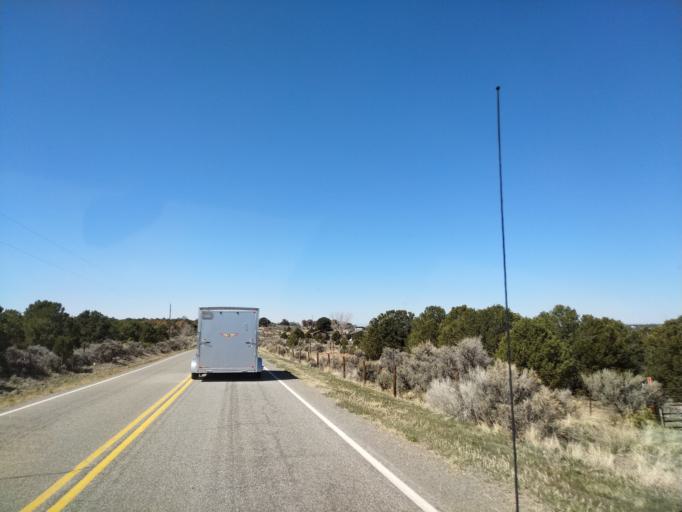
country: US
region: Colorado
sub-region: Mesa County
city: Redlands
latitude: 38.9938
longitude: -108.7226
